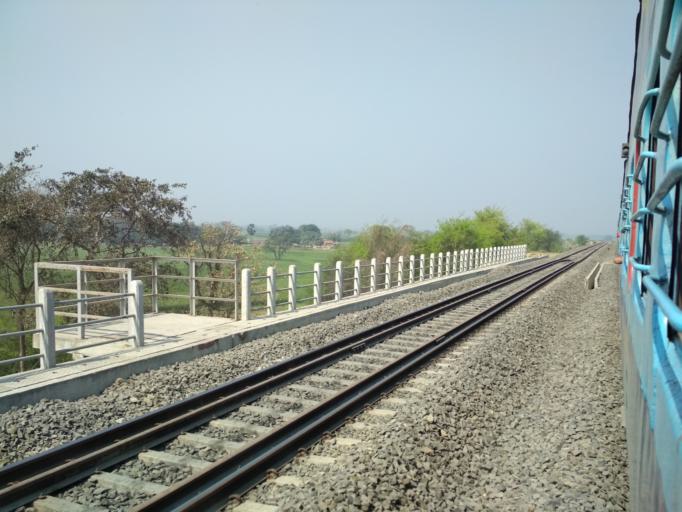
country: IN
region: Bihar
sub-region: Munger
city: Munger
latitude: 25.4379
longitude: 86.4334
